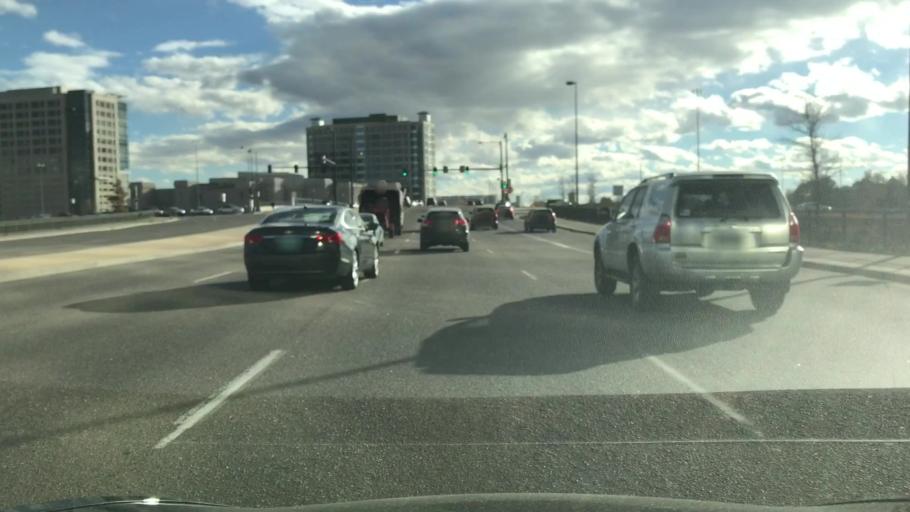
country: US
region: Colorado
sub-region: Arapahoe County
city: Glendale
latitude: 39.6848
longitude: -104.9409
